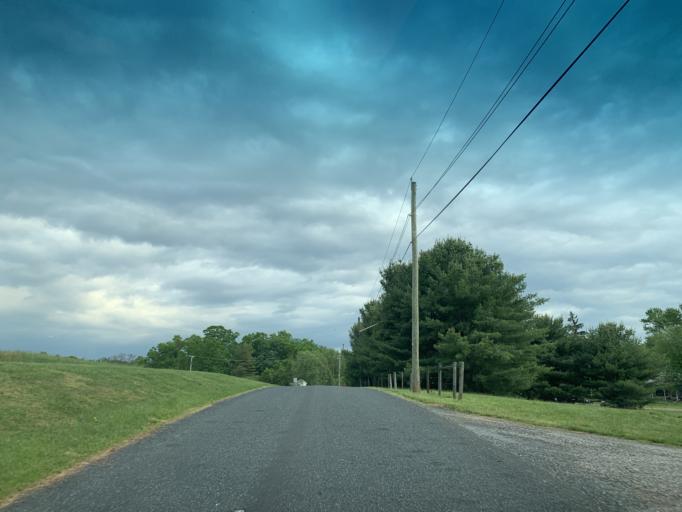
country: US
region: Pennsylvania
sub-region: York County
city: Susquehanna Trails
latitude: 39.6726
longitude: -76.2583
